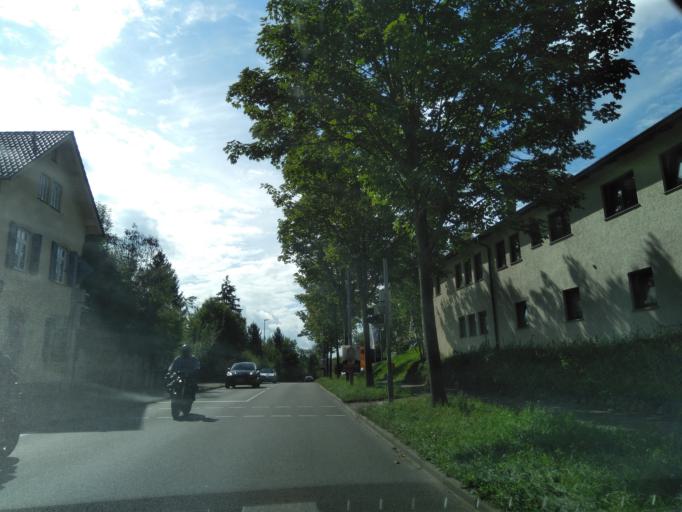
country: DE
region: Baden-Wuerttemberg
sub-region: Regierungsbezirk Stuttgart
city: Besigheim
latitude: 48.9704
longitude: 9.1428
